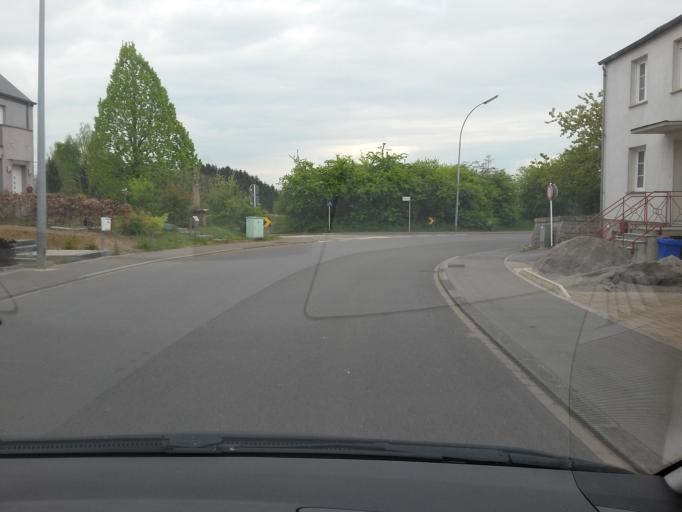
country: LU
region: Luxembourg
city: Hautcharage
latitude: 49.5790
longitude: 5.9114
